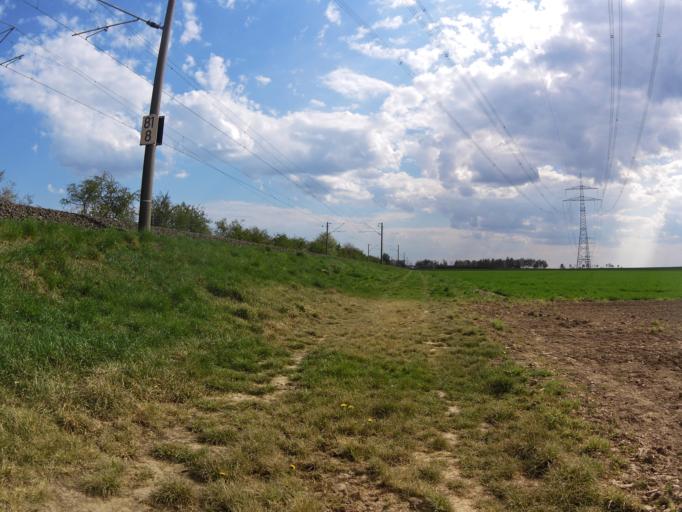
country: DE
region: Bavaria
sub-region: Regierungsbezirk Unterfranken
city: Oberpleichfeld
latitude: 49.8636
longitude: 10.1004
